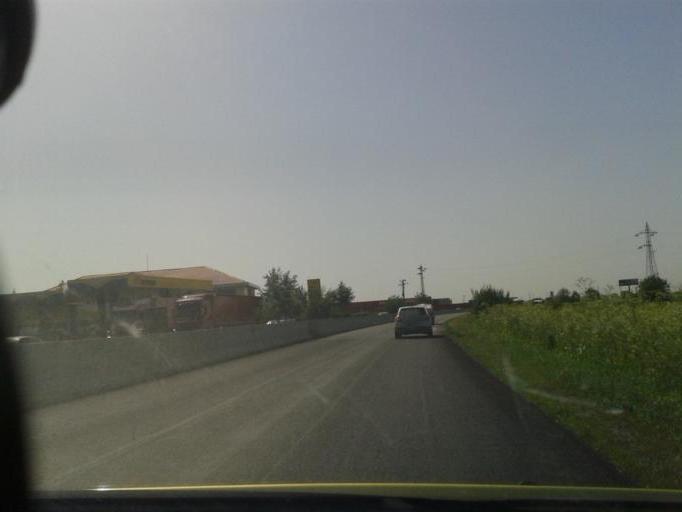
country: RO
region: Prahova
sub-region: Comuna Paulesti
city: Paulesti
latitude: 44.9681
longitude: 25.9617
